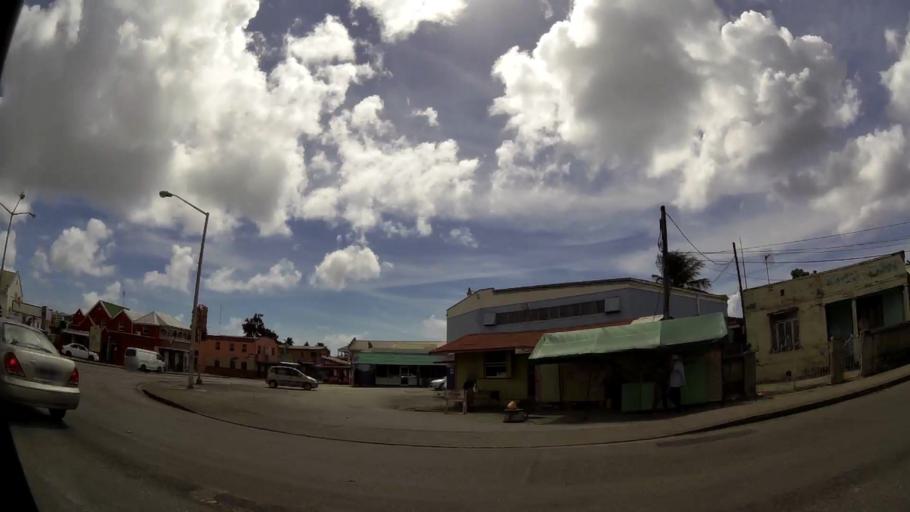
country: BB
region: Saint Michael
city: Bridgetown
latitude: 13.1047
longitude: -59.6176
